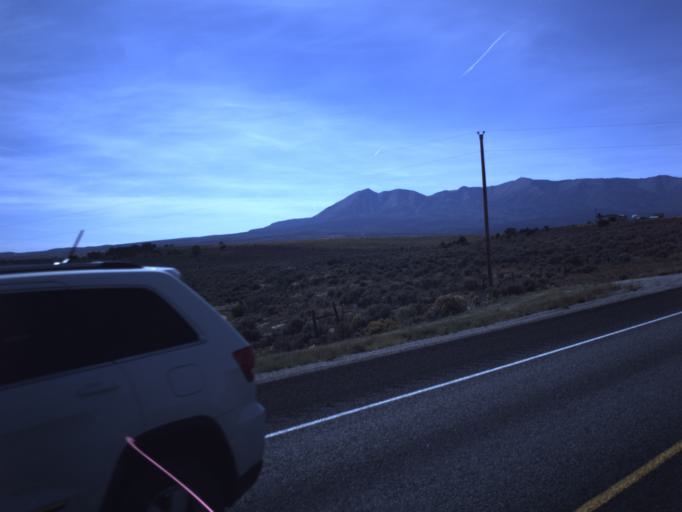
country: US
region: Utah
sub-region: San Juan County
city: Monticello
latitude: 37.8701
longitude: -109.2514
